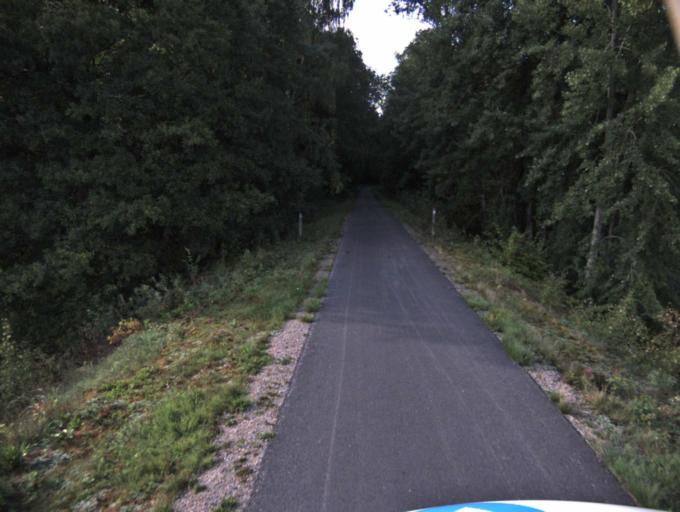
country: SE
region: Vaestra Goetaland
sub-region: Ulricehamns Kommun
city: Ulricehamn
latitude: 57.7305
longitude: 13.4097
